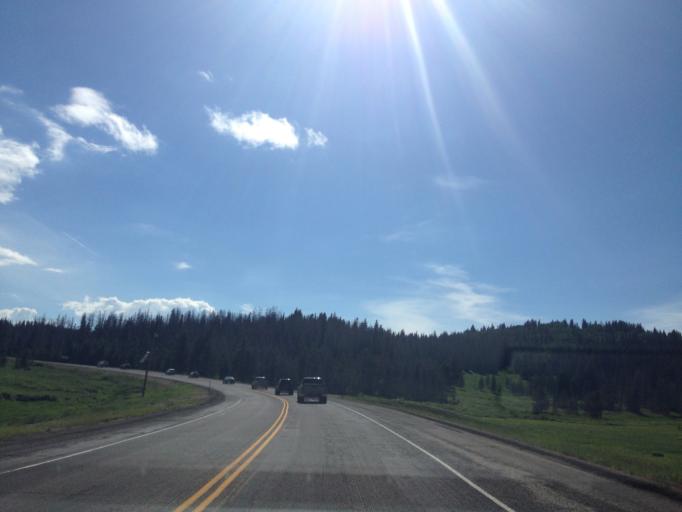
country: US
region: Colorado
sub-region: Routt County
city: Steamboat Springs
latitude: 40.3758
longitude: -106.7331
